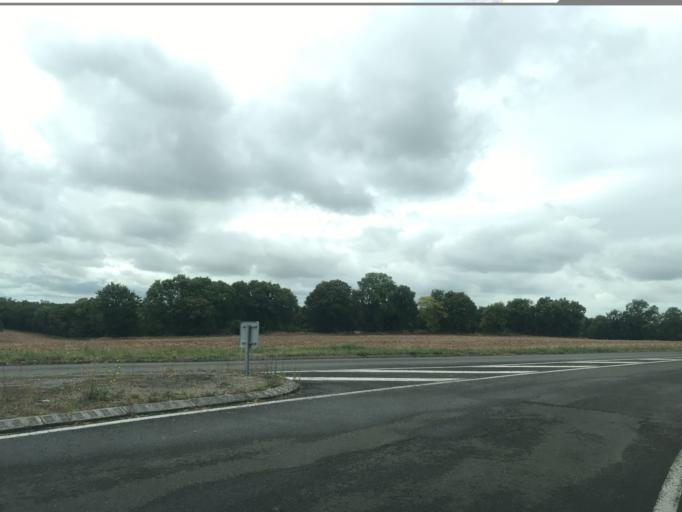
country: FR
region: Poitou-Charentes
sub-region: Departement de la Charente
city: Puymoyen
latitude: 45.6129
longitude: 0.1941
